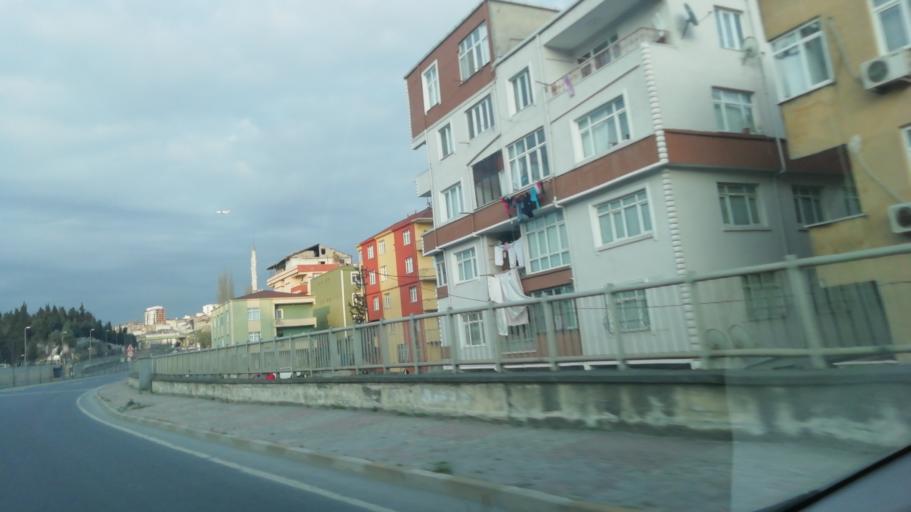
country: TR
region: Istanbul
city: Mahmutbey
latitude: 41.0166
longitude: 28.7767
